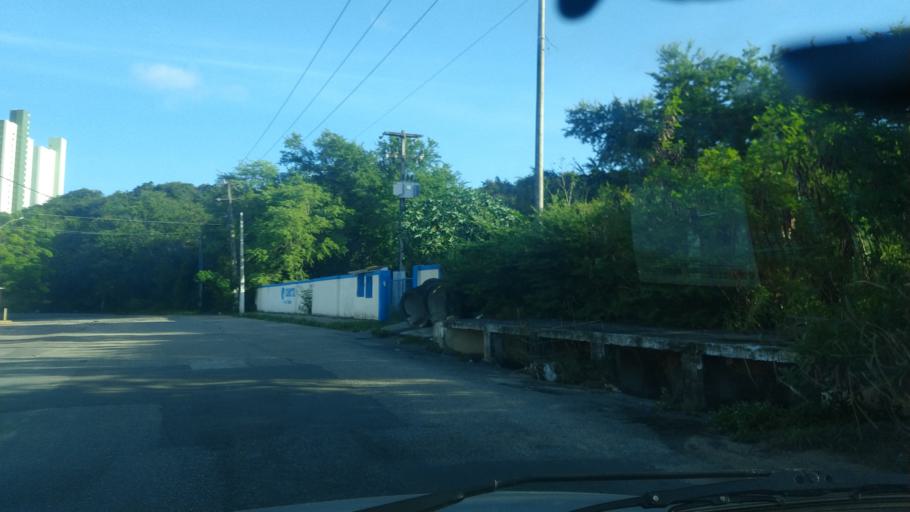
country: BR
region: Rio Grande do Norte
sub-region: Natal
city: Natal
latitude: -5.8773
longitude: -35.1856
